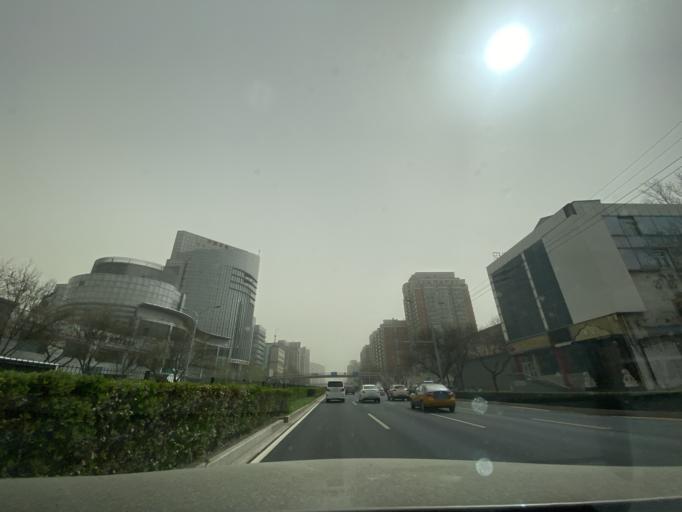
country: CN
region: Beijing
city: Sijiqing
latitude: 39.9443
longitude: 116.2946
